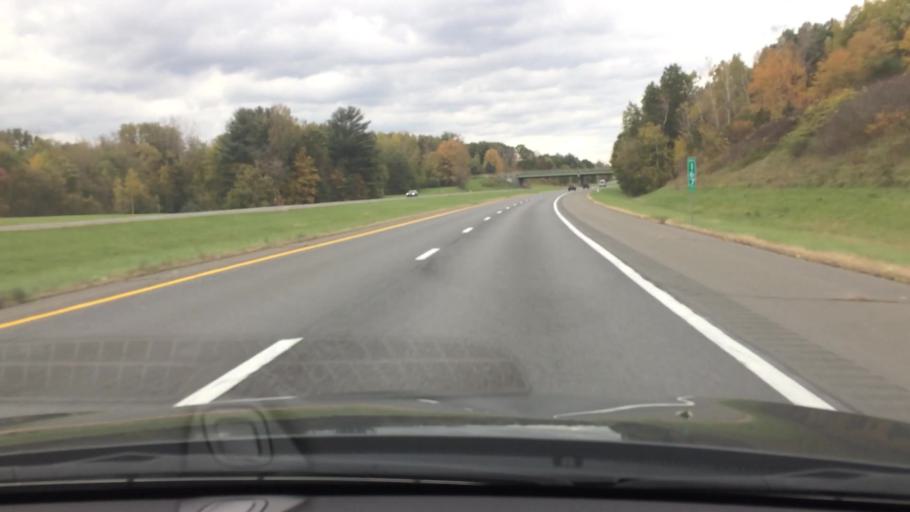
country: US
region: New York
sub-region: Rensselaer County
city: East Greenbush
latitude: 42.5295
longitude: -73.6875
